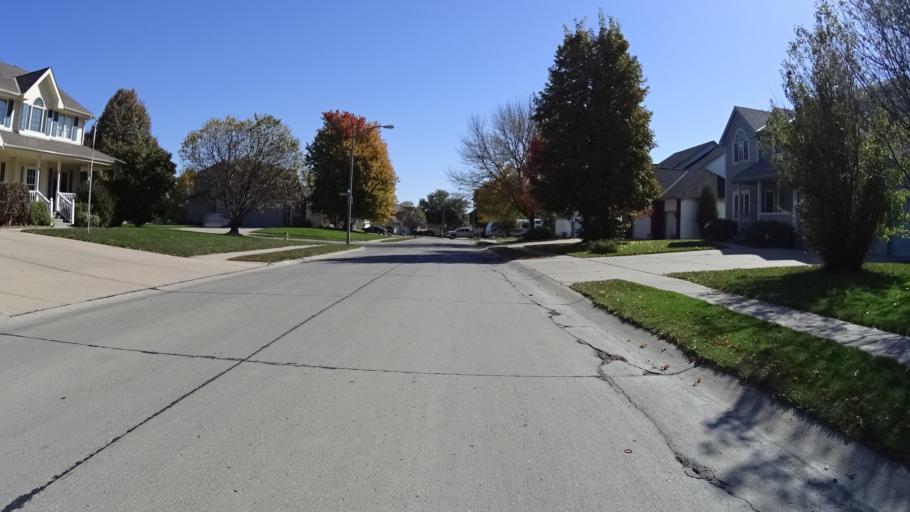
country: US
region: Nebraska
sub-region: Sarpy County
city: La Vista
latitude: 41.1731
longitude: -96.0257
